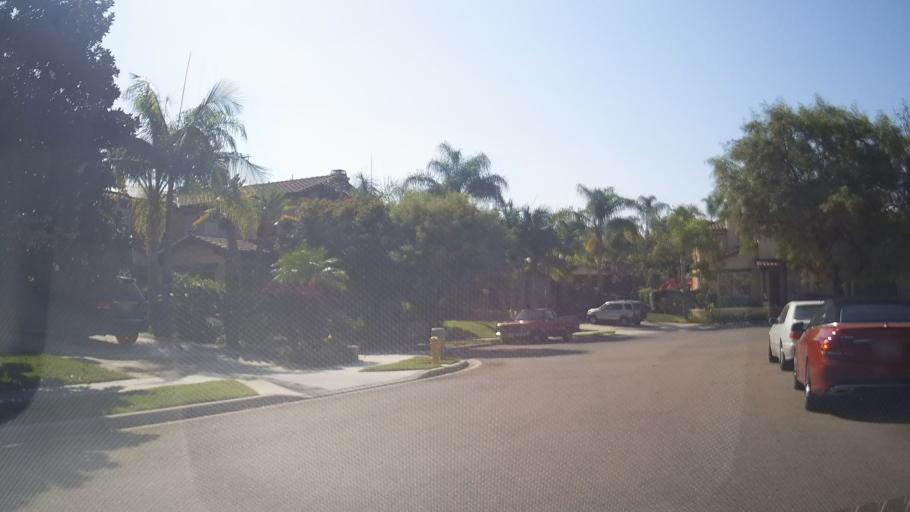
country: US
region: California
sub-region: San Diego County
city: Fairbanks Ranch
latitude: 33.0076
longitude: -117.1201
